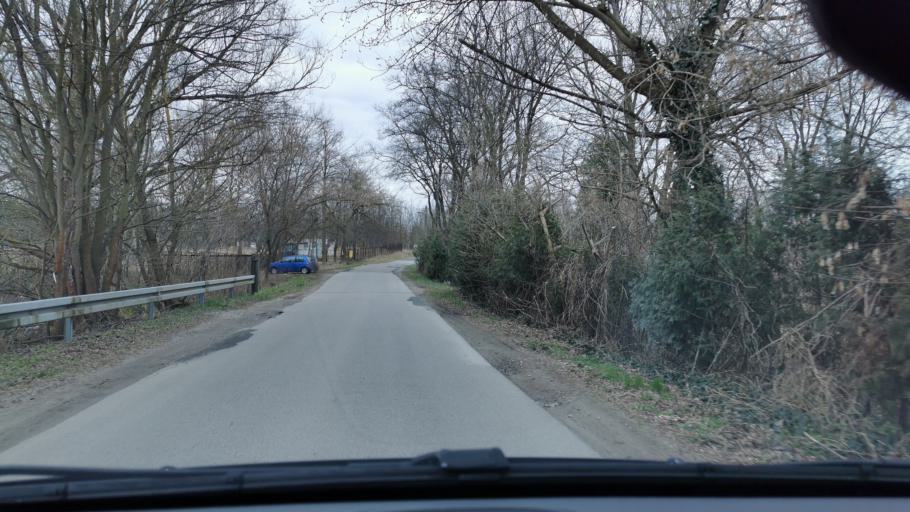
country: PL
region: Masovian Voivodeship
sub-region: Powiat zyrardowski
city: Radziejowice
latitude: 52.0105
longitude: 20.5206
